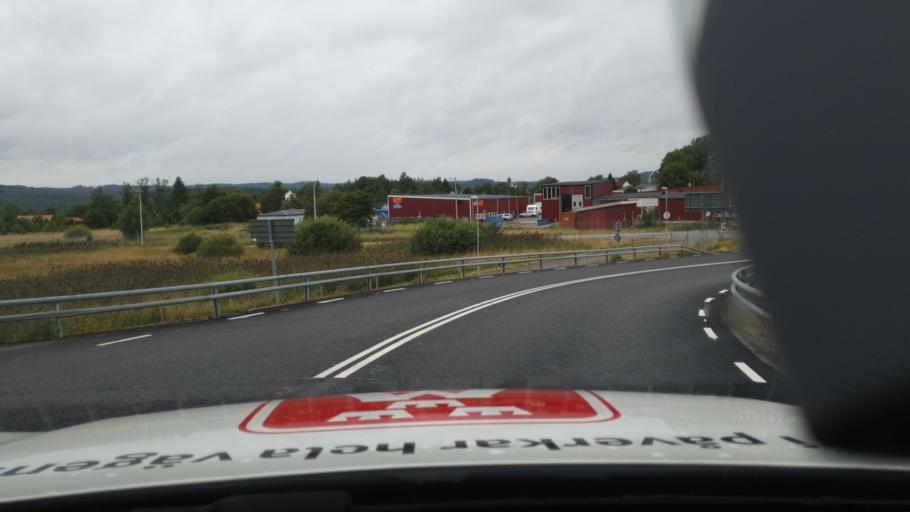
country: SE
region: Vaestra Goetaland
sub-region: Lilla Edets Kommun
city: Lilla Edet
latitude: 58.1247
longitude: 12.1367
